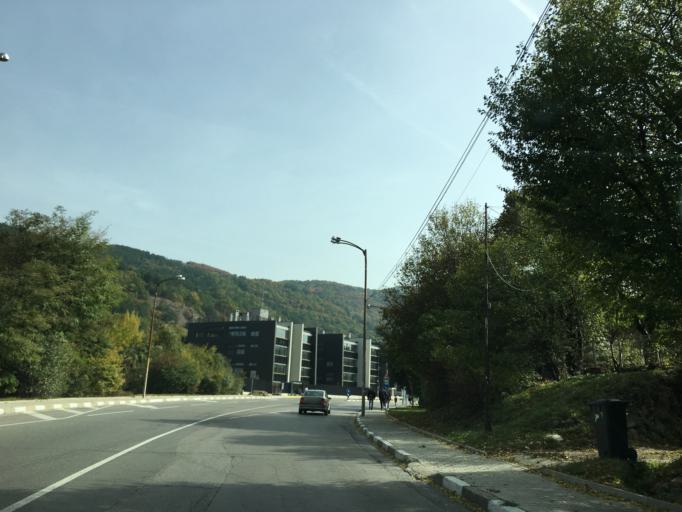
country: BG
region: Sofia-Capital
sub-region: Stolichna Obshtina
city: Sofia
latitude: 42.5965
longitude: 23.4123
